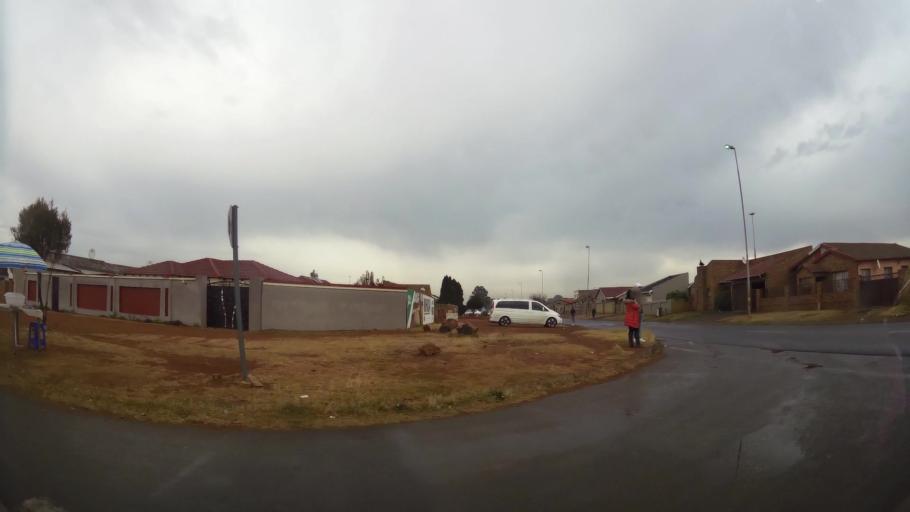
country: ZA
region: Gauteng
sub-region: Ekurhuleni Metropolitan Municipality
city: Germiston
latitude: -26.3286
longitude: 28.1976
